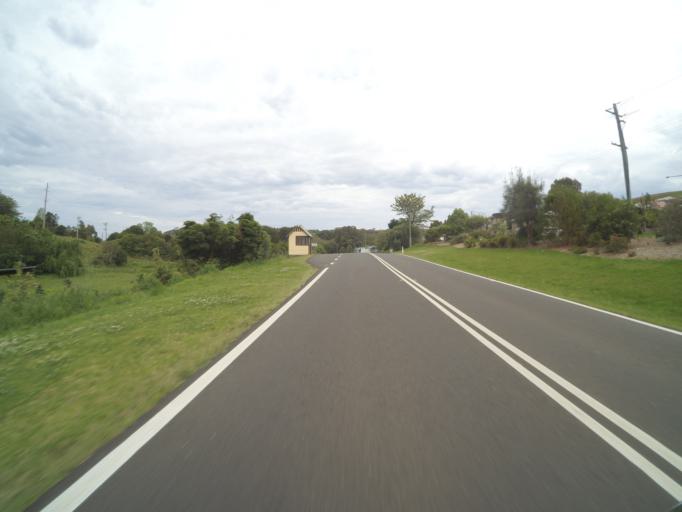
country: AU
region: New South Wales
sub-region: Kiama
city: Kiama
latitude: -34.6629
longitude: 150.8413
